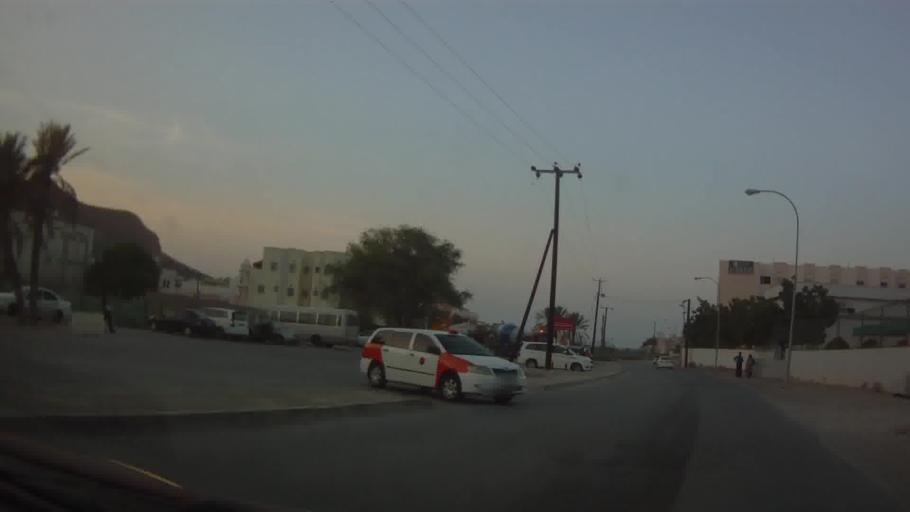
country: OM
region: Muhafazat Masqat
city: Muscat
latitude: 23.6275
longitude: 58.5417
